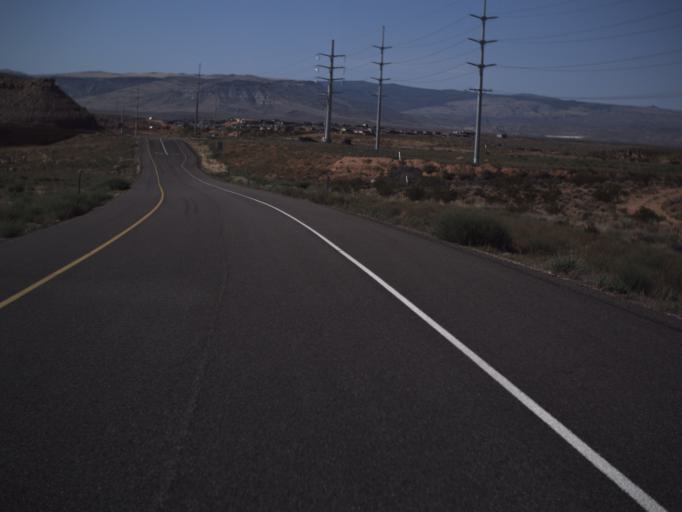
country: US
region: Utah
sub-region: Washington County
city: Washington
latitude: 37.0177
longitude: -113.4928
